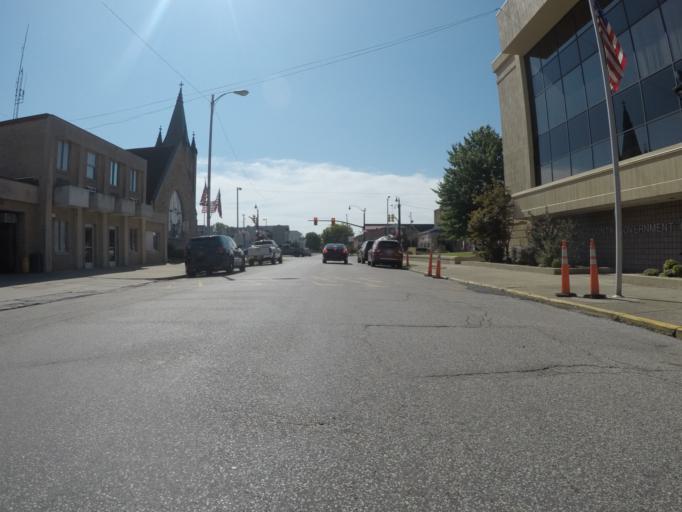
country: US
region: Ohio
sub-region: Lawrence County
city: Ironton
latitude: 38.5363
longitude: -82.6832
